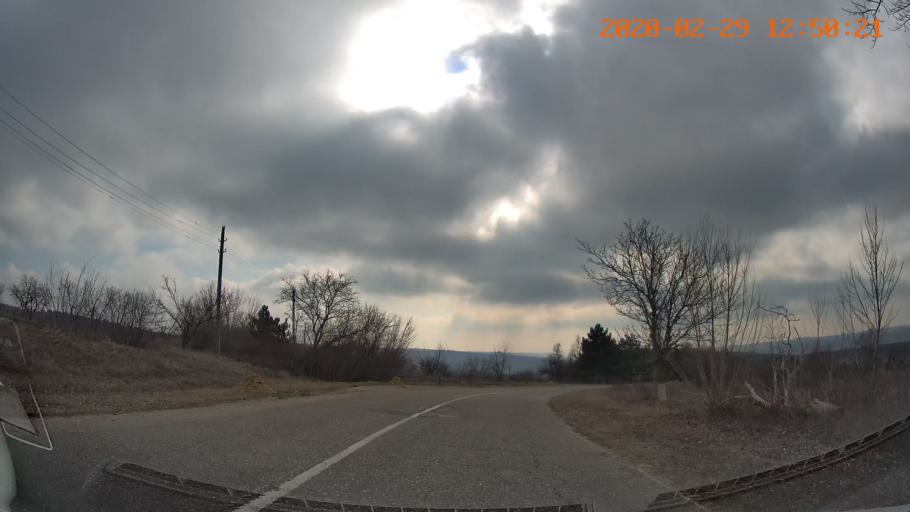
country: MD
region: Telenesti
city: Camenca
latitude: 48.1249
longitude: 28.7399
